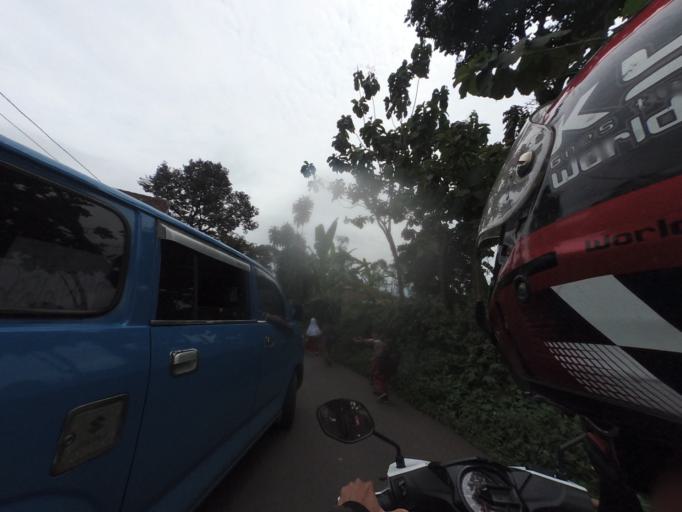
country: ID
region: West Java
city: Bogor
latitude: -6.6376
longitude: 106.7442
